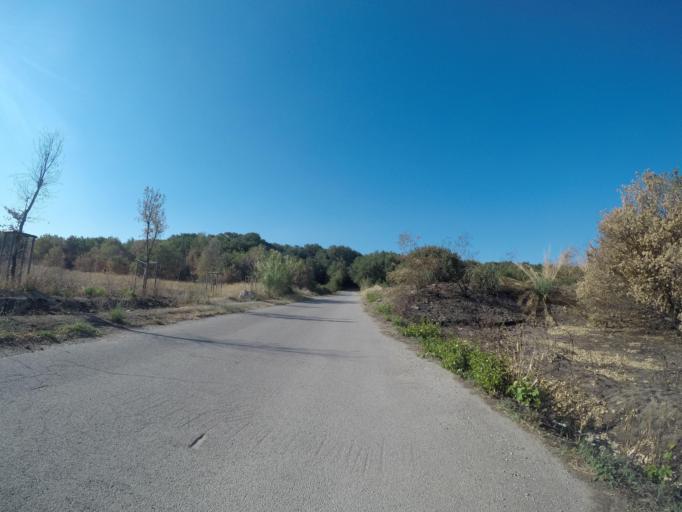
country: FR
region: Languedoc-Roussillon
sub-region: Departement des Pyrenees-Orientales
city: Pezilla-la-Riviere
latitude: 42.6826
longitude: 2.7655
